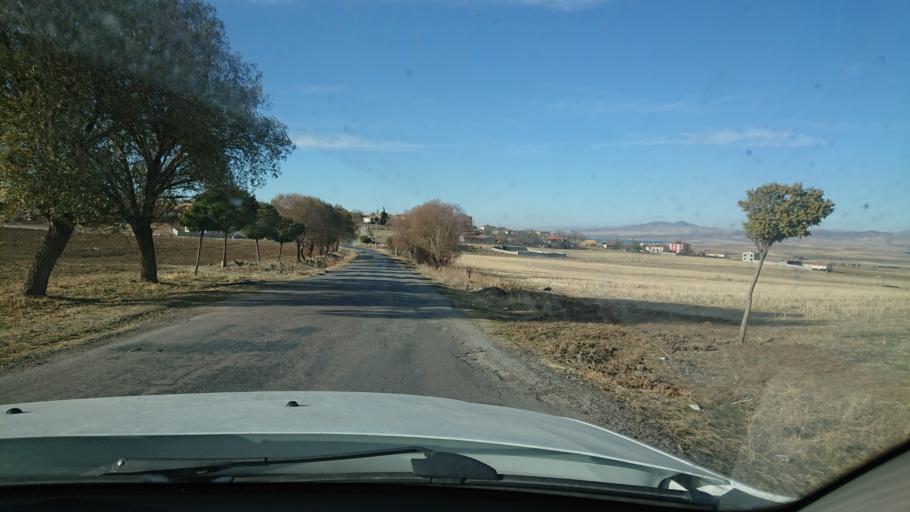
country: TR
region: Aksaray
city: Sariyahsi
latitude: 38.9763
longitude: 33.8566
